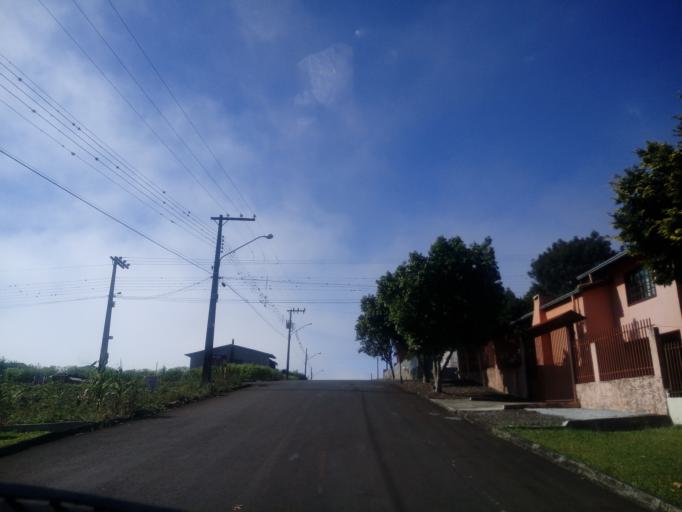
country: BR
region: Santa Catarina
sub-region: Chapeco
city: Chapeco
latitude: -27.0756
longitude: -52.6147
